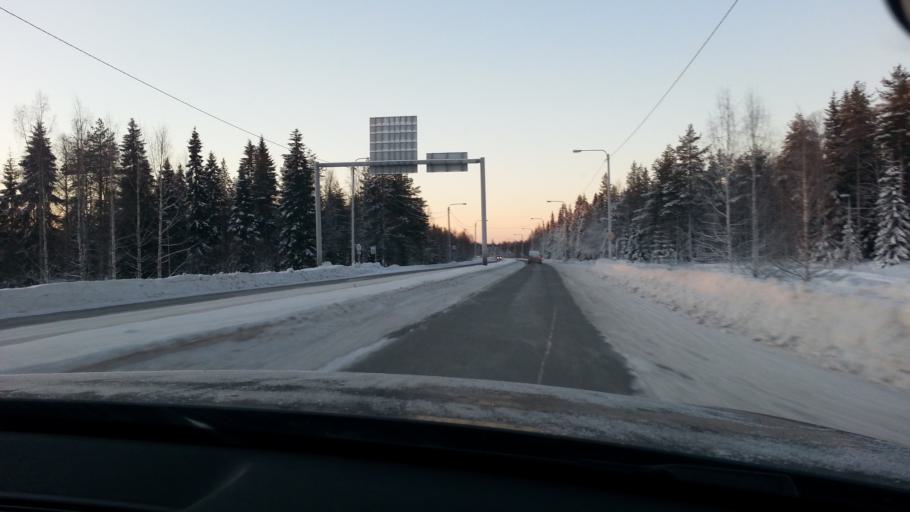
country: FI
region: Lapland
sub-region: Rovaniemi
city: Rovaniemi
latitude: 66.5426
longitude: 25.8176
